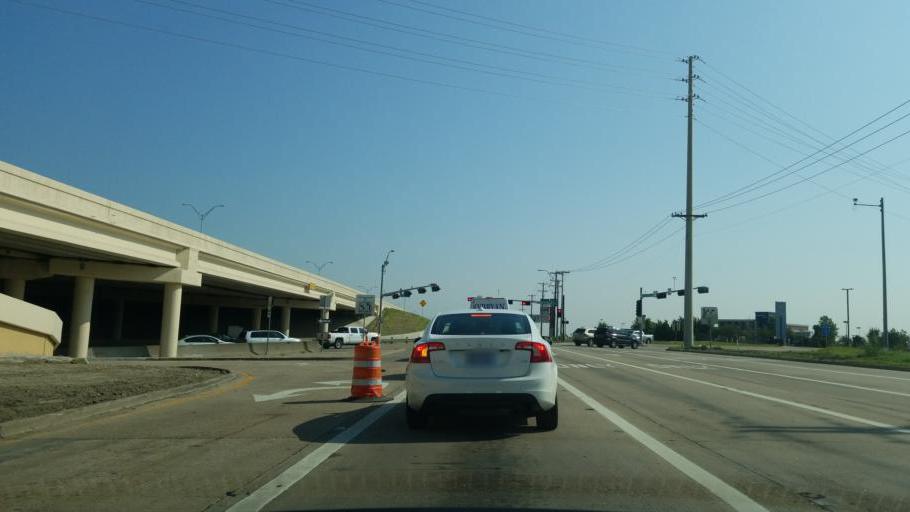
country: US
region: Texas
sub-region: Collin County
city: Allen
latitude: 33.1293
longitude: -96.6597
